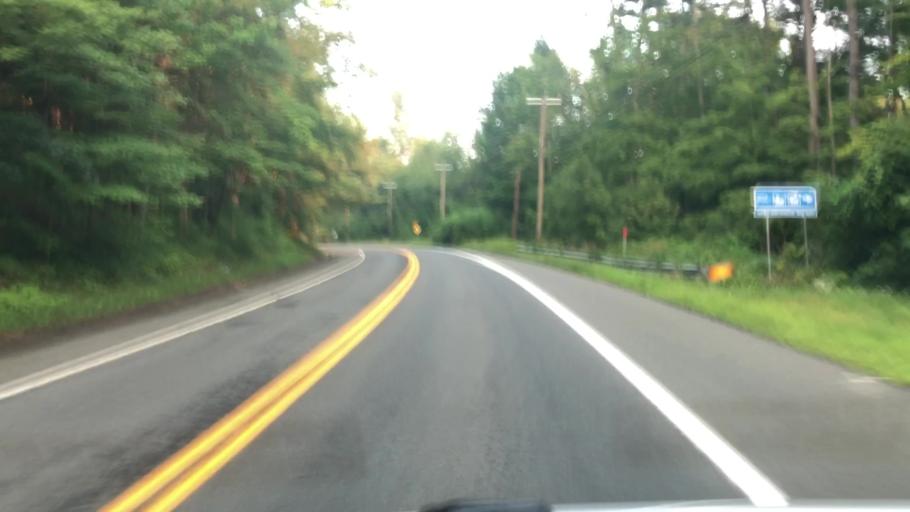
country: US
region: Massachusetts
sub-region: Franklin County
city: Shelburne
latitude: 42.6127
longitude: -72.6638
